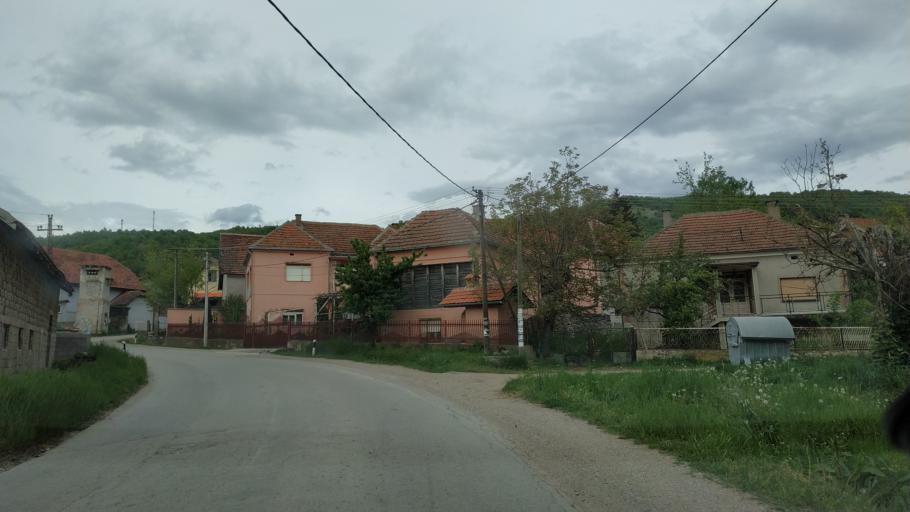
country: RS
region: Central Serbia
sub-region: Nisavski Okrug
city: Aleksinac
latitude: 43.6336
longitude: 21.7183
